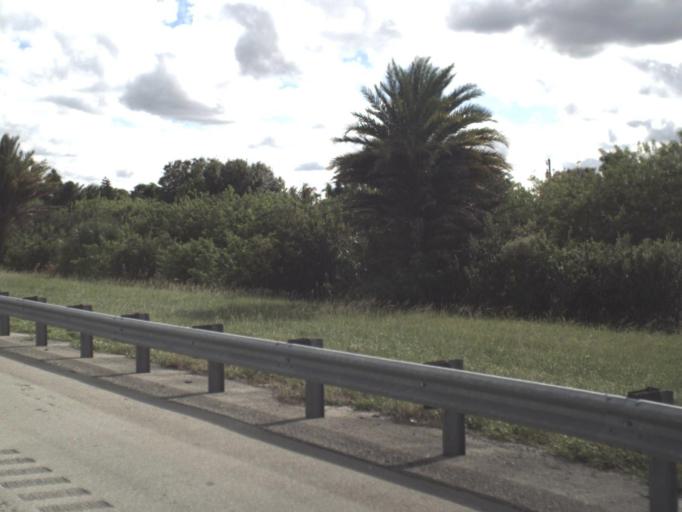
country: US
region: Florida
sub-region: Saint Lucie County
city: Port Saint Lucie
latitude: 27.2949
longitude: -80.3706
